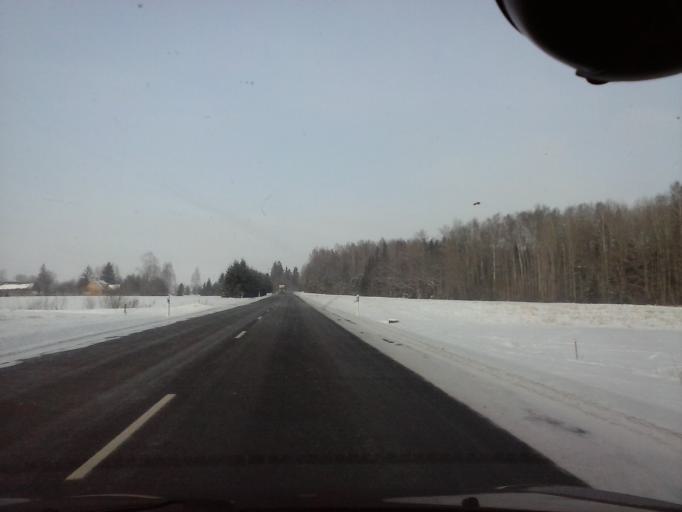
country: EE
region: Viljandimaa
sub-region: Abja vald
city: Abja-Paluoja
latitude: 58.3029
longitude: 25.2993
